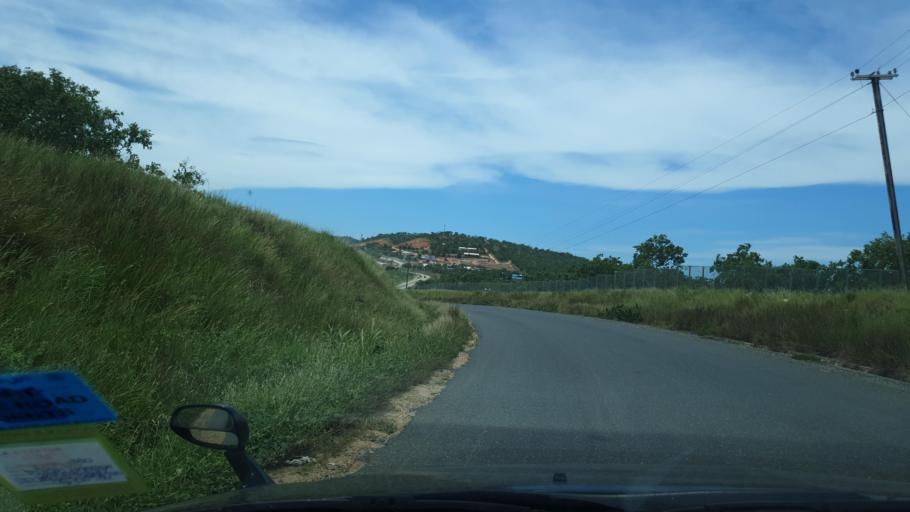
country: PG
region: National Capital
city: Port Moresby
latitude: -9.4418
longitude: 147.0760
